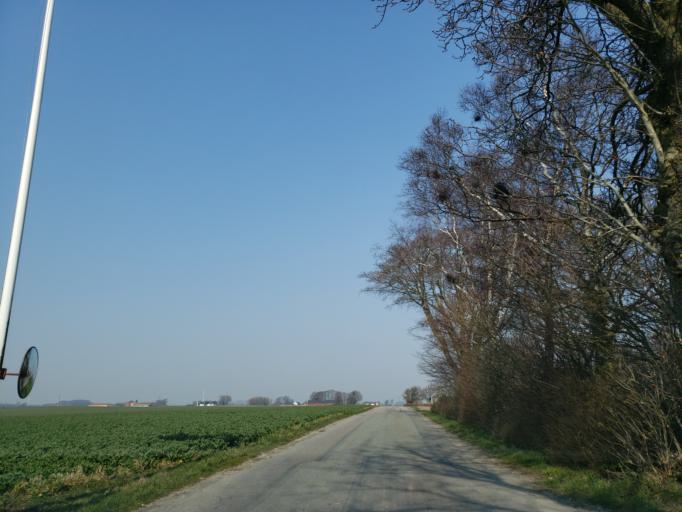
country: SE
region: Skane
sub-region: Simrishamns Kommun
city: Simrishamn
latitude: 55.4467
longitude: 14.2178
